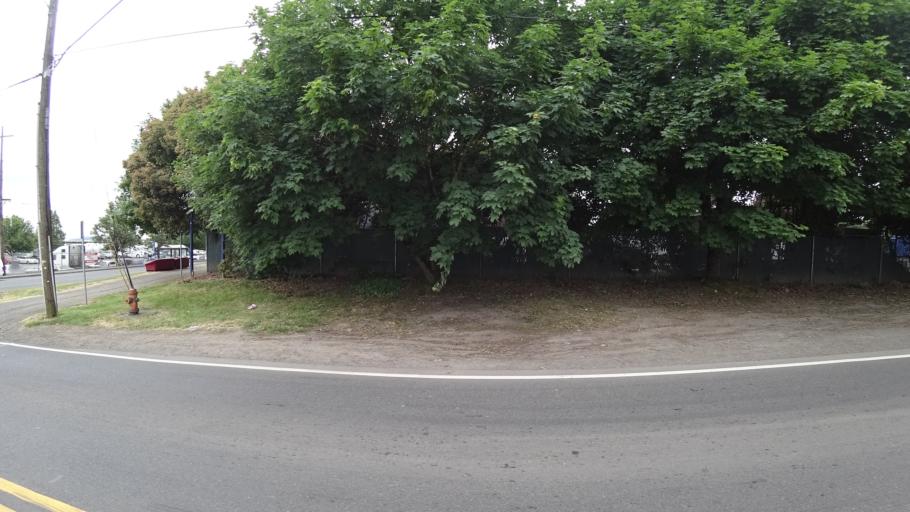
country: US
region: Washington
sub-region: Clark County
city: Vancouver
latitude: 45.5902
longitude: -122.6626
